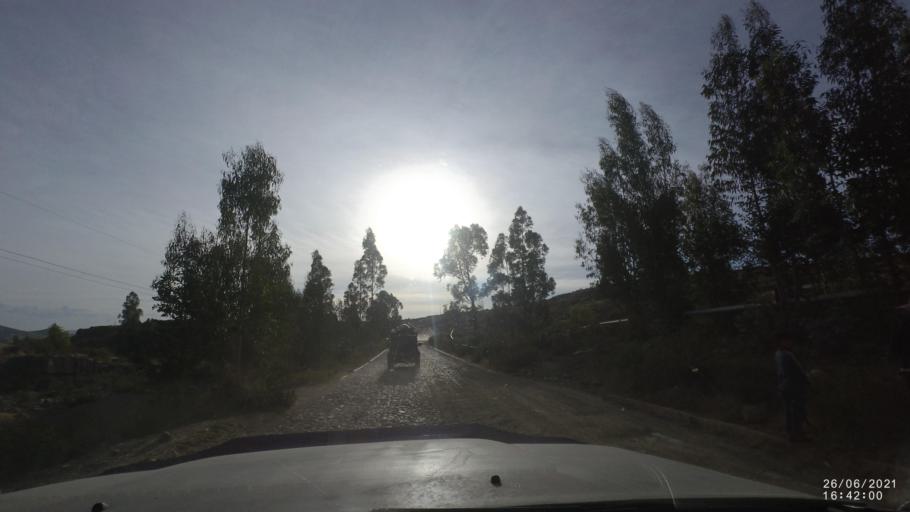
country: BO
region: Cochabamba
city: Arani
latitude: -17.7651
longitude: -65.8239
